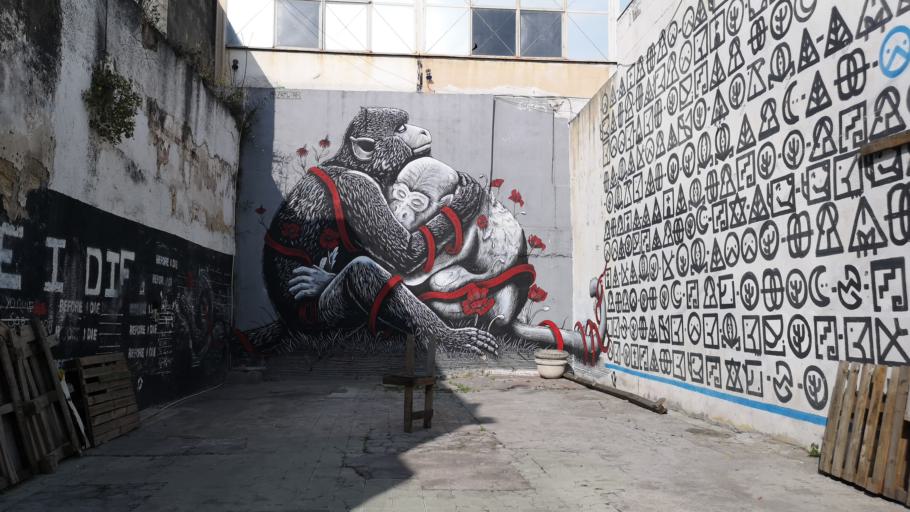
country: MX
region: Nuevo Leon
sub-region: Monterrey
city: Monterrey
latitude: 25.6661
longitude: -100.3076
